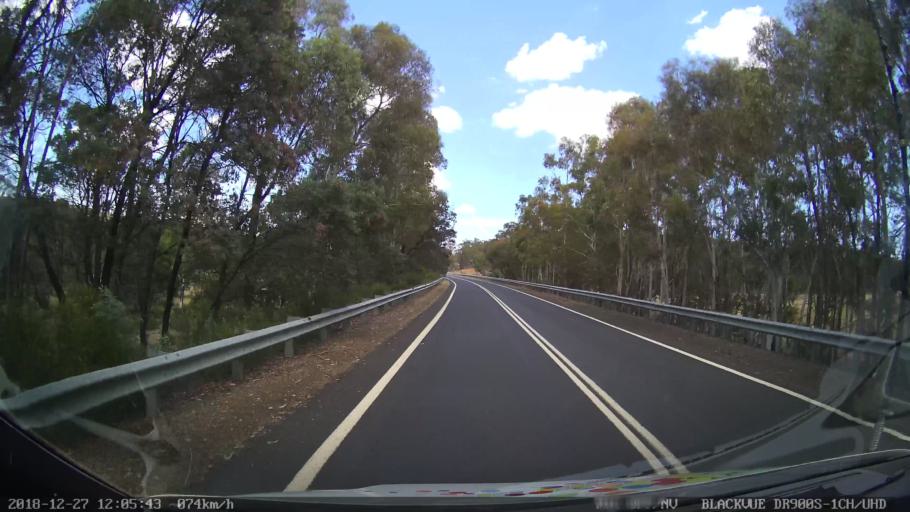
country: AU
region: New South Wales
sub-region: Blayney
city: Blayney
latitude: -33.8035
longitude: 149.3356
